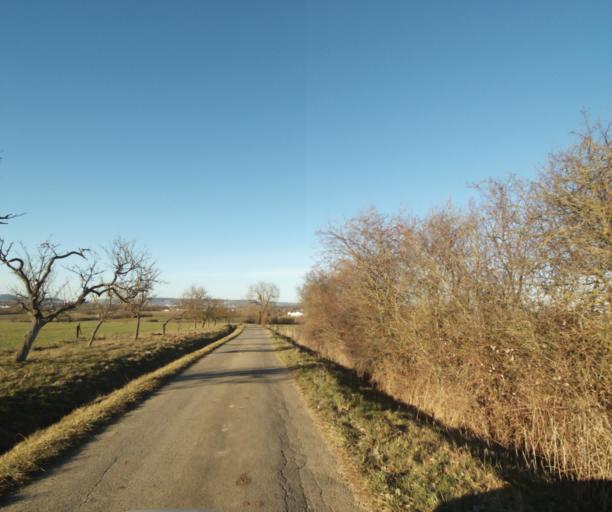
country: FR
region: Lorraine
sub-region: Departement de Meurthe-et-Moselle
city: Laneuveville-devant-Nancy
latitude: 48.6388
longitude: 6.2312
